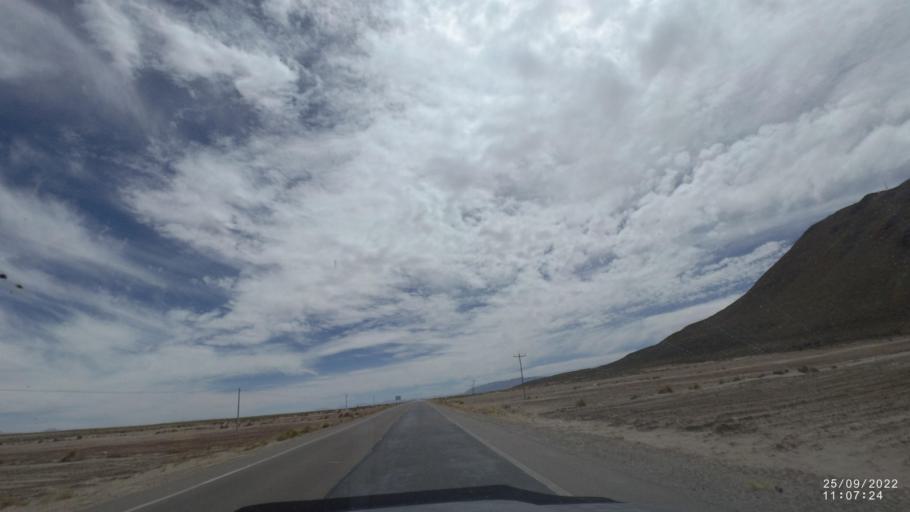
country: BO
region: Oruro
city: Challapata
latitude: -19.3445
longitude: -66.8547
